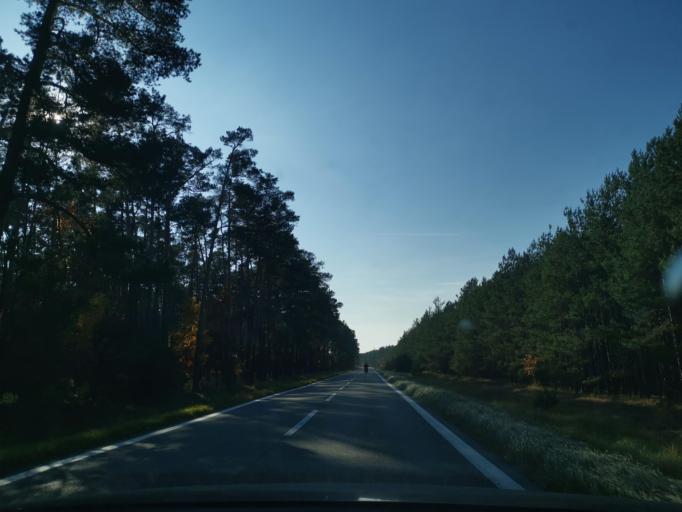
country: SK
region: Bratislavsky
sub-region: Okres Malacky
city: Malacky
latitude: 48.4966
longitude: 17.0948
